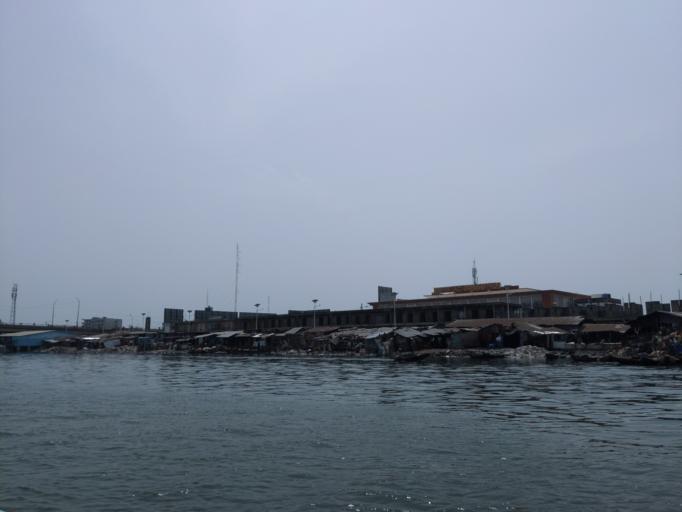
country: BJ
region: Littoral
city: Cotonou
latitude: 6.3730
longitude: 2.4362
